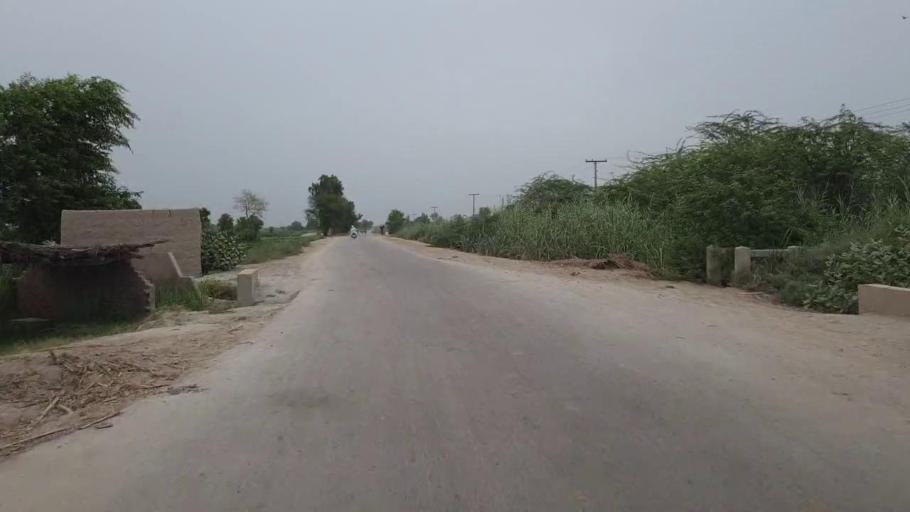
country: PK
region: Sindh
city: Bandhi
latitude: 26.5517
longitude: 68.2129
